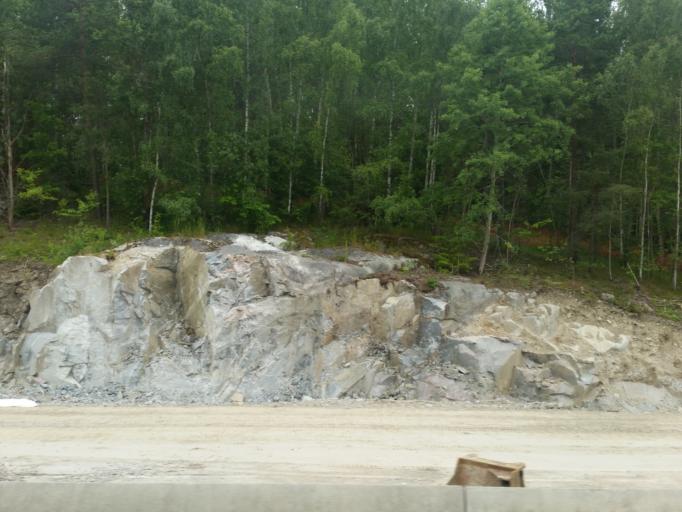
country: SE
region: Stockholm
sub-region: Stockholms Kommun
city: Kista
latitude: 59.4172
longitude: 17.9062
